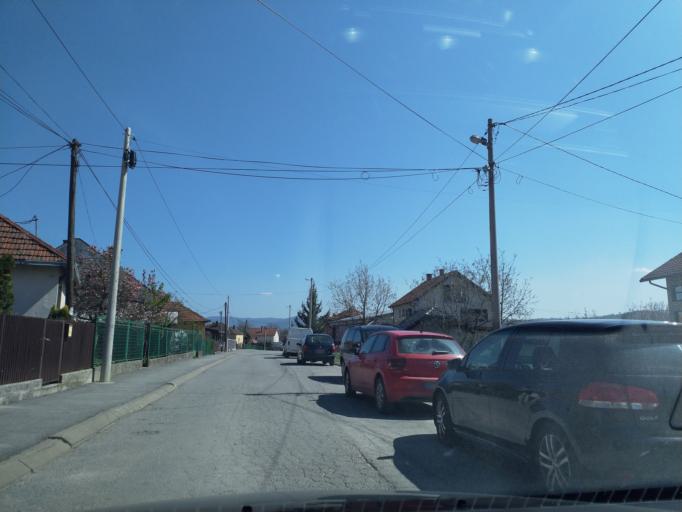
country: RS
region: Central Serbia
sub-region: Kolubarski Okrug
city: Valjevo
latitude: 44.2789
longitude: 19.8693
